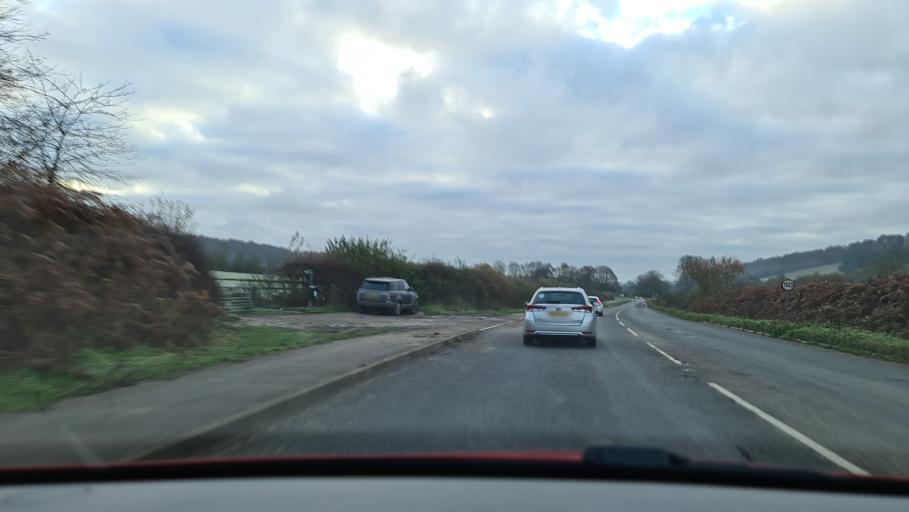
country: GB
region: England
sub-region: Buckinghamshire
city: Princes Risborough
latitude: 51.6693
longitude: -0.8133
